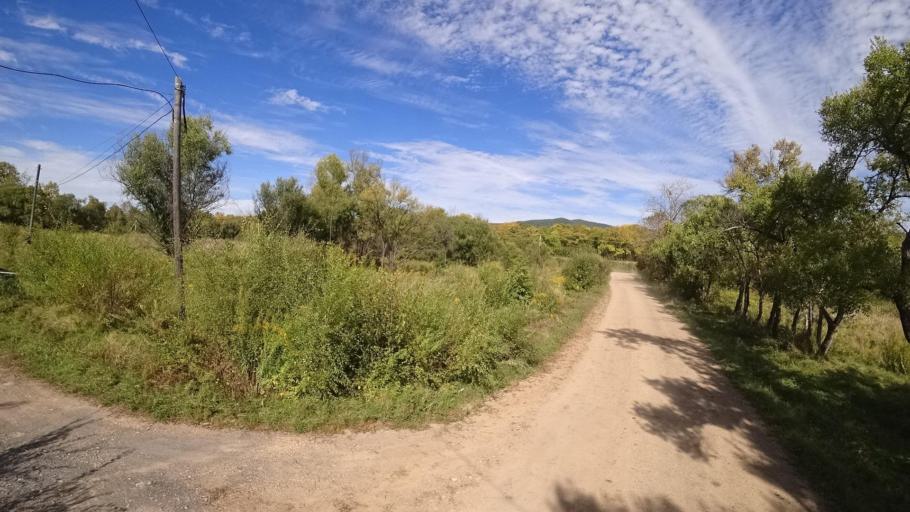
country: RU
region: Primorskiy
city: Yakovlevka
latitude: 44.3909
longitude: 133.6080
